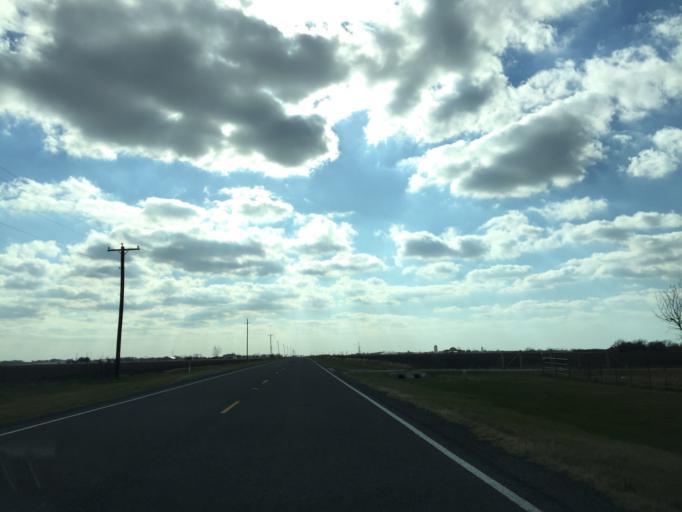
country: US
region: Texas
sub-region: Williamson County
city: Granger
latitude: 30.6609
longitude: -97.3701
